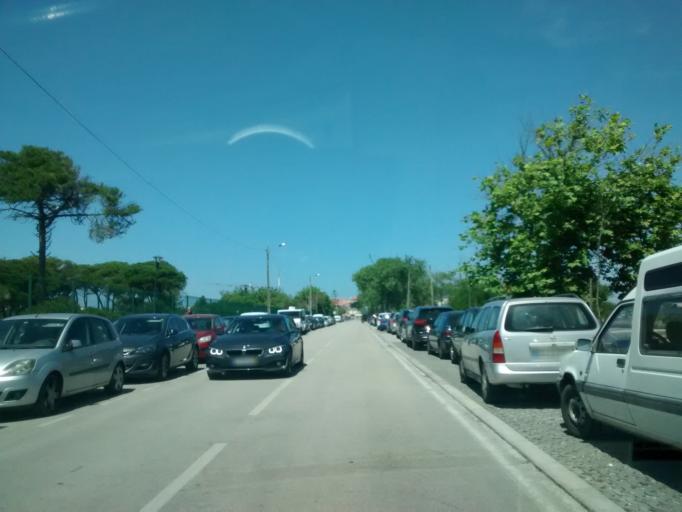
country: PT
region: Coimbra
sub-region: Mira
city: Mira
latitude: 40.4478
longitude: -8.8003
